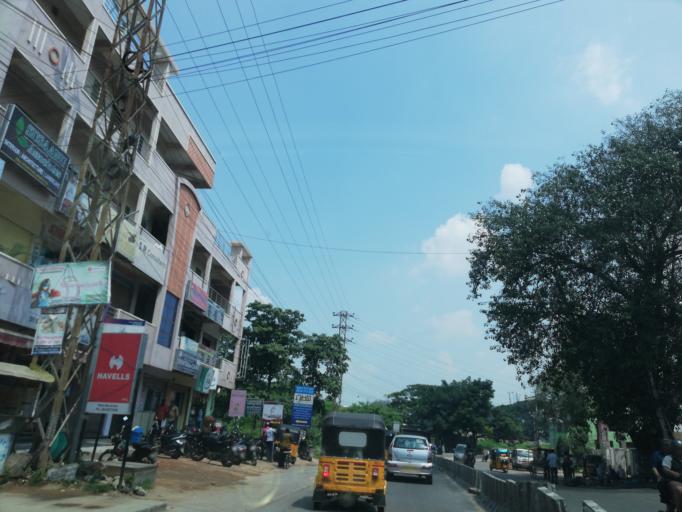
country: IN
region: Telangana
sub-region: Medak
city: Serilingampalle
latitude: 17.4833
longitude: 78.3204
